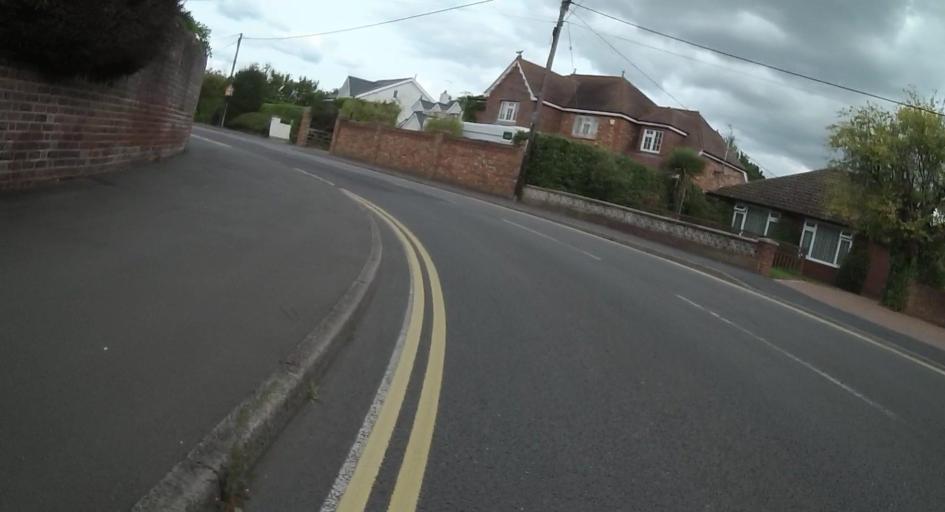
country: GB
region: England
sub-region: Surrey
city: Knaphill
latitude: 51.3397
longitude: -0.6341
